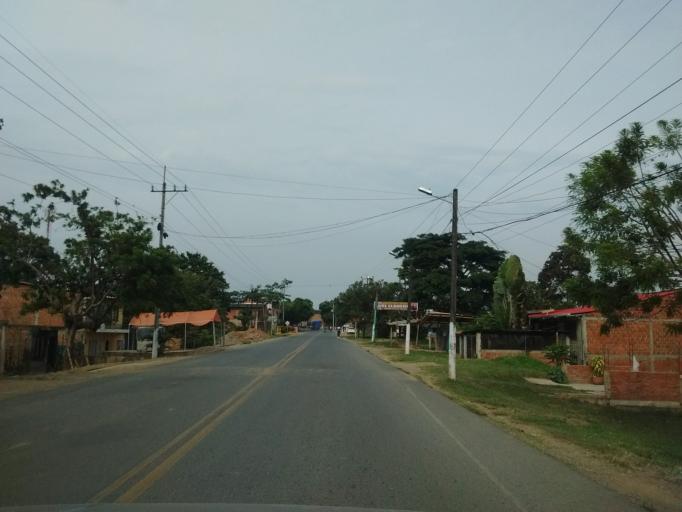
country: CO
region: Cauca
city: Puerto Tejada
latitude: 3.1759
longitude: -76.4567
